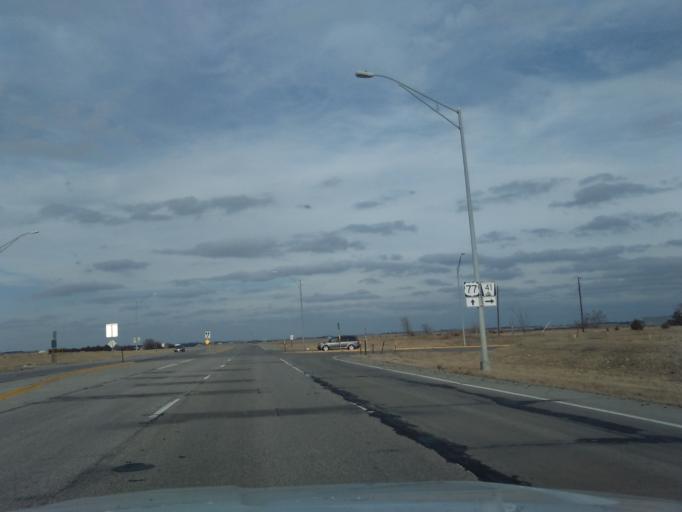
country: US
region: Nebraska
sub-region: Lancaster County
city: Hickman
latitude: 40.4666
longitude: -96.7103
